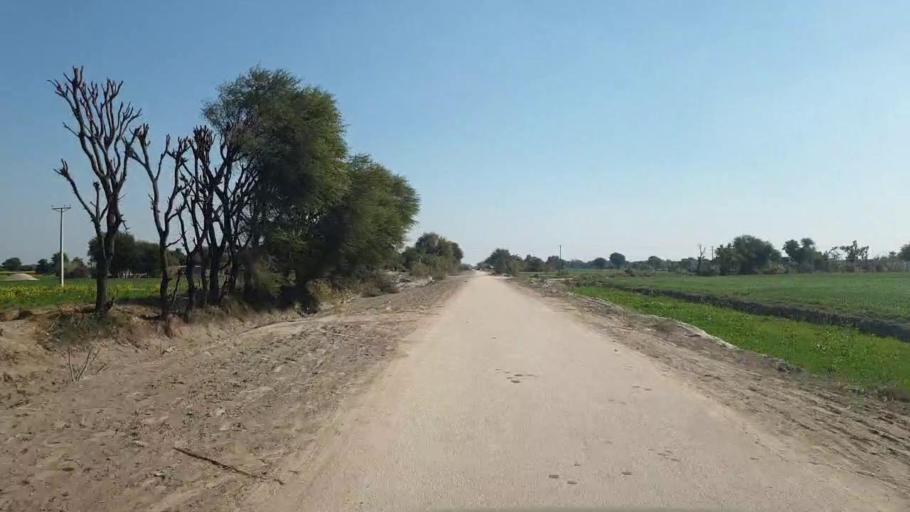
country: PK
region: Sindh
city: Shahpur Chakar
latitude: 26.1366
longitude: 68.6621
